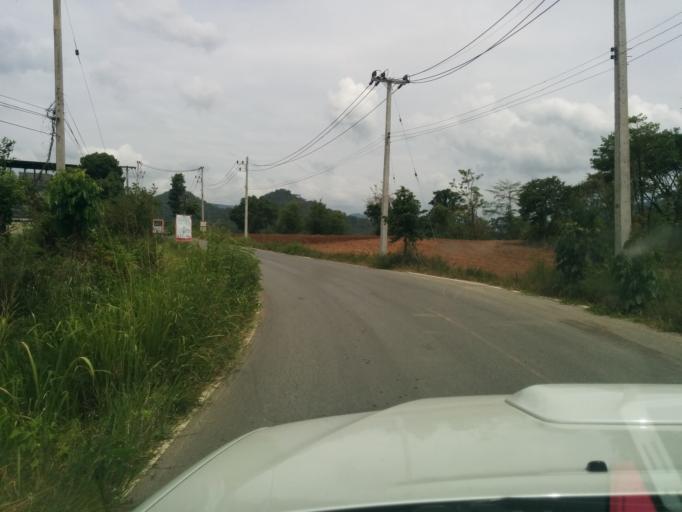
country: TH
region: Sara Buri
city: Muak Lek
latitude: 14.5748
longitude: 101.2386
